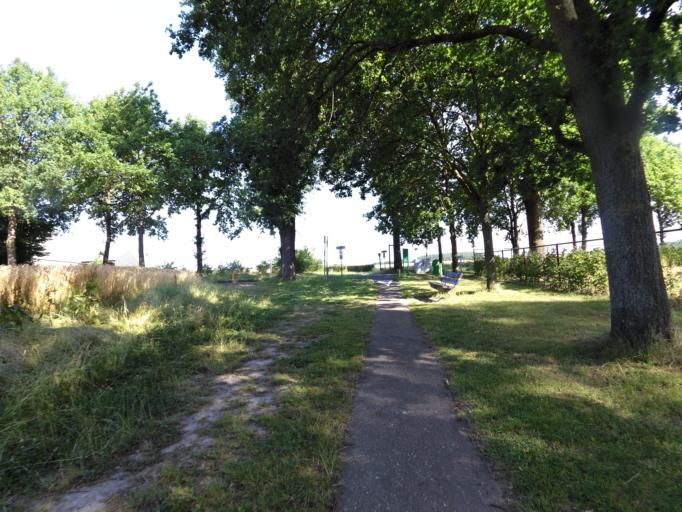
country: NL
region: Limburg
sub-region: Gemeente Voerendaal
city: Voerendaal
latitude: 50.8887
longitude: 5.9241
